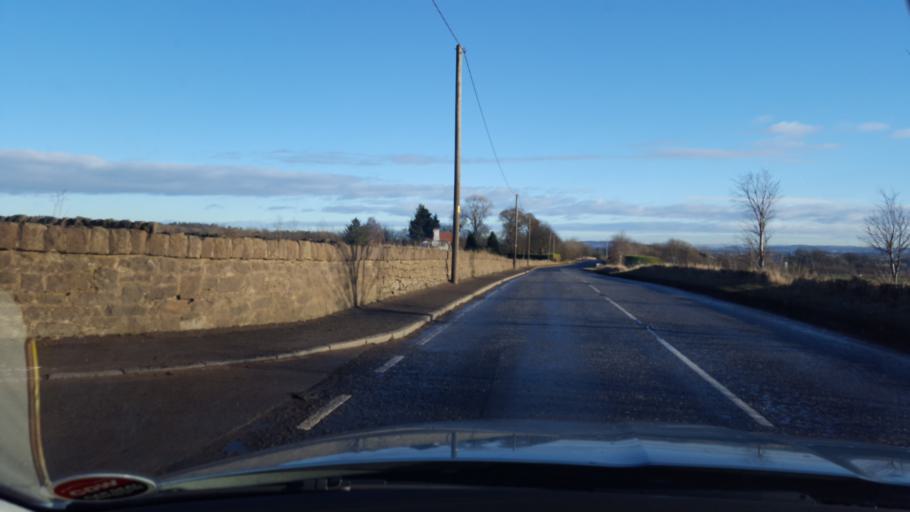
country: GB
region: Scotland
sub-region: West Lothian
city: Broxburn
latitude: 55.9617
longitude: -3.4474
